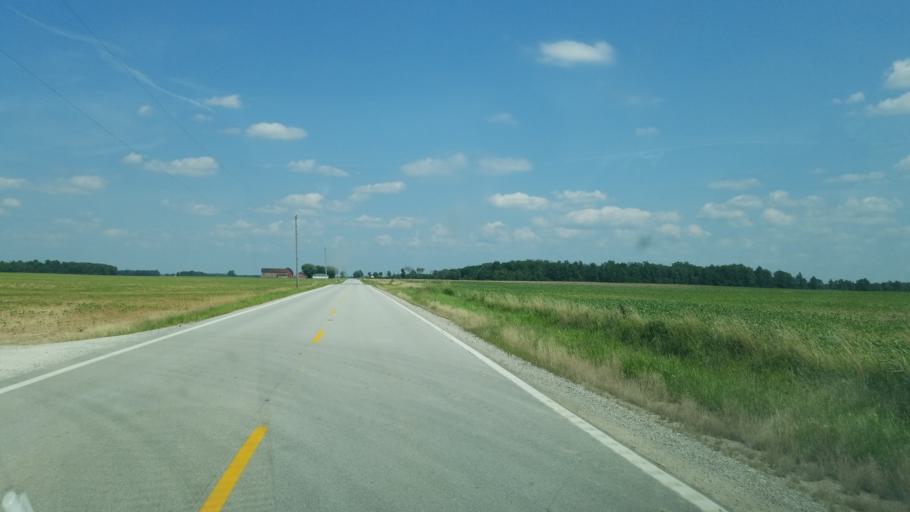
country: US
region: Ohio
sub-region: Huron County
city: Willard
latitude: 41.1243
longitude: -82.8546
